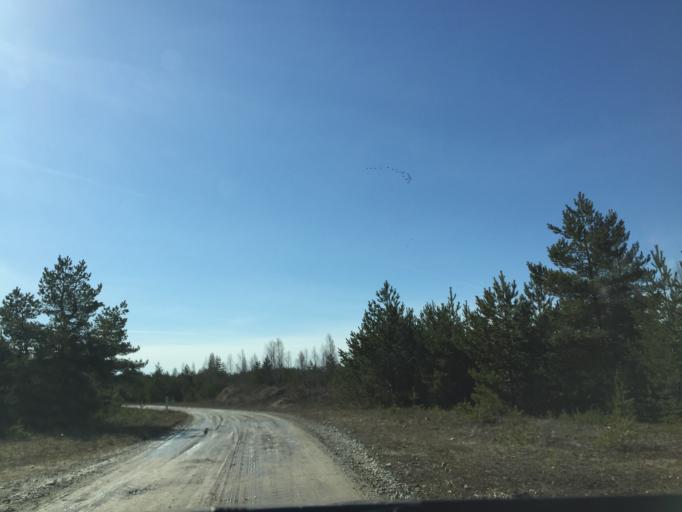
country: EE
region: Laeaene
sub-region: Haapsalu linn
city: Haapsalu
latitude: 58.6328
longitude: 23.5252
